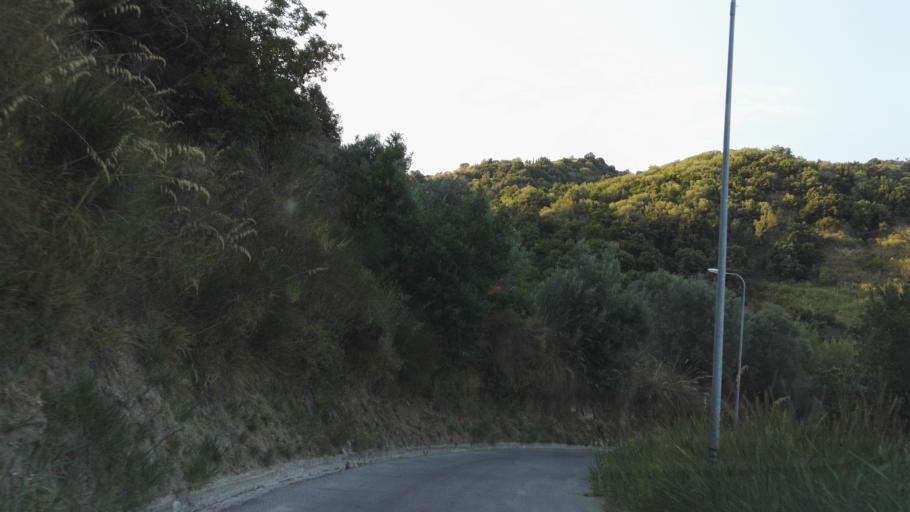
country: IT
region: Calabria
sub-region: Provincia di Reggio Calabria
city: Placanica
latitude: 38.4077
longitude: 16.4242
